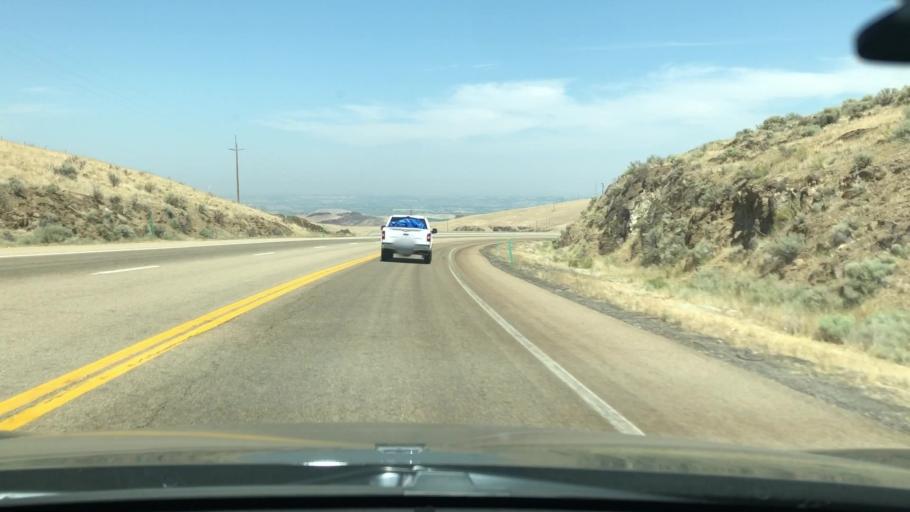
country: US
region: Idaho
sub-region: Owyhee County
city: Marsing
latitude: 43.4145
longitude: -116.8622
